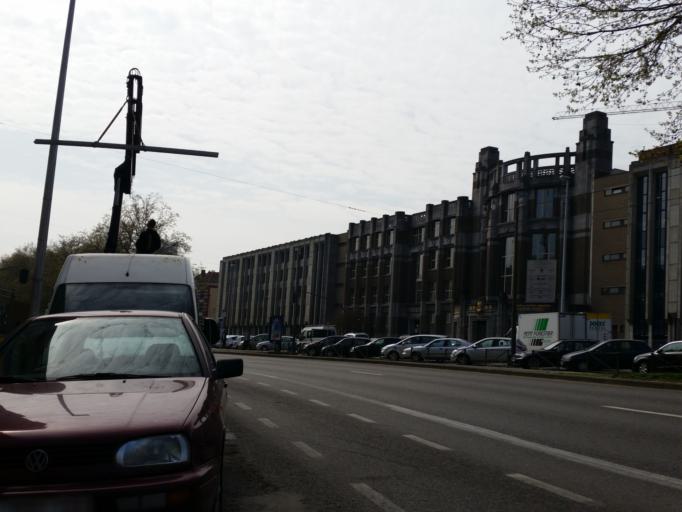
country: BE
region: Brussels Capital
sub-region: Bruxelles-Capitale
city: Brussels
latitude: 50.8482
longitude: 4.3382
